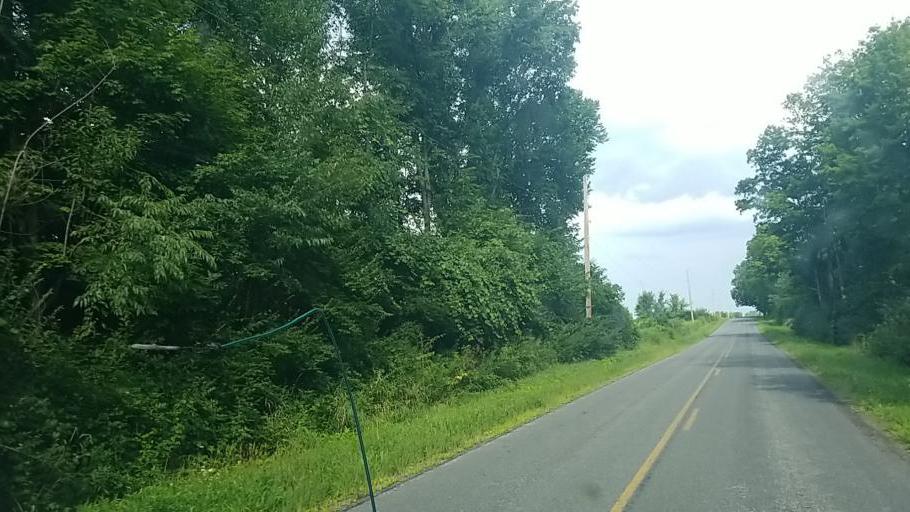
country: US
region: Ohio
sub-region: Medina County
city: Westfield Center
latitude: 41.0124
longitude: -81.9467
